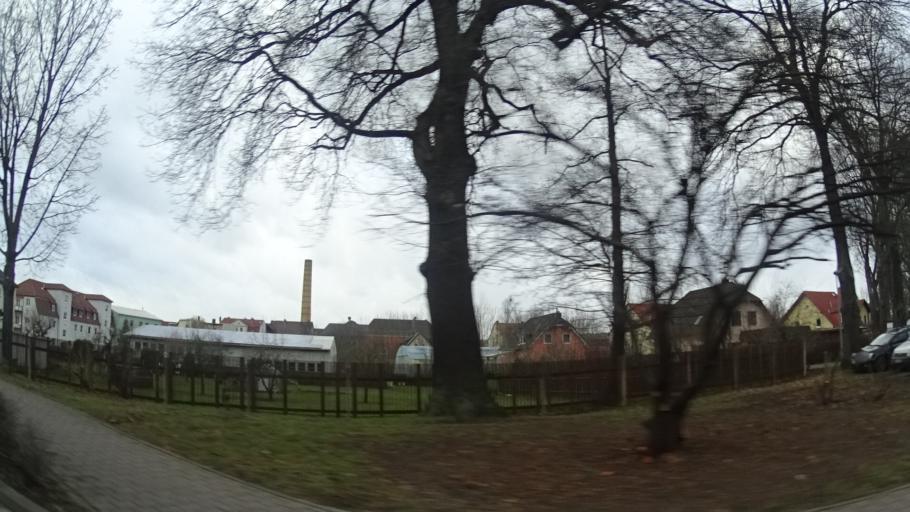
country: DE
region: Thuringia
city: Neustadt (Orla)
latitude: 50.7371
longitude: 11.7501
